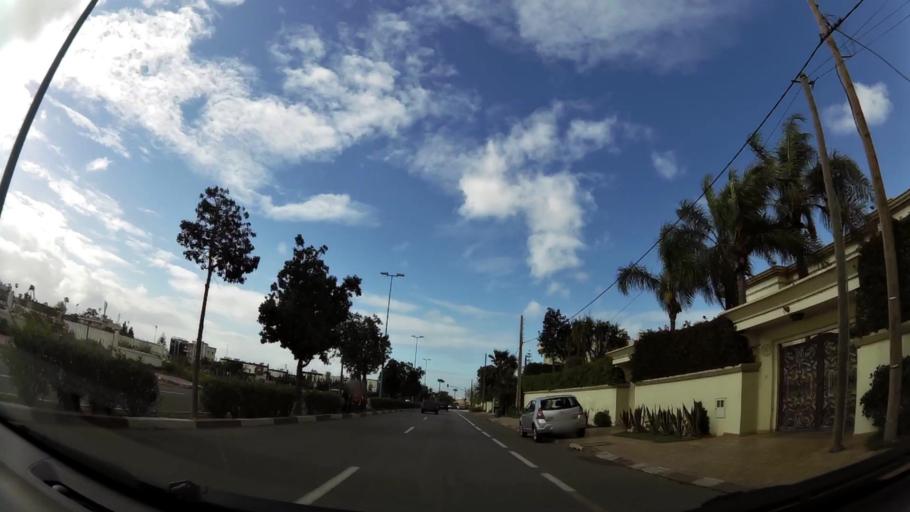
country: MA
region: Grand Casablanca
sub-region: Casablanca
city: Casablanca
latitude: 33.5482
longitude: -7.6221
